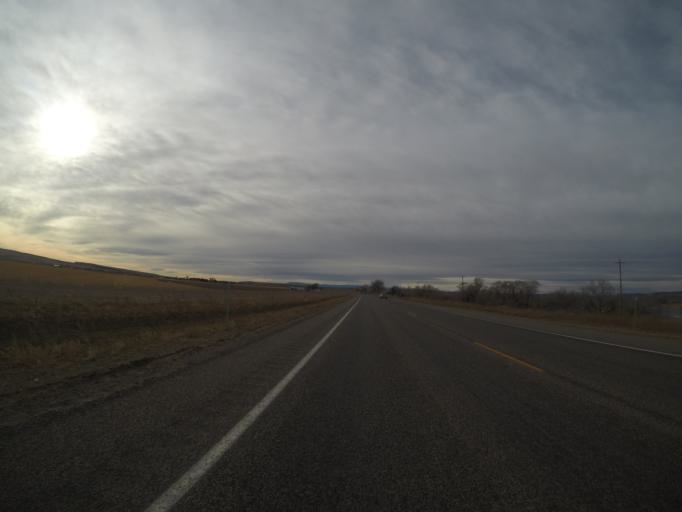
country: US
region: Montana
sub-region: Yellowstone County
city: Laurel
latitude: 45.6236
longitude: -108.8073
